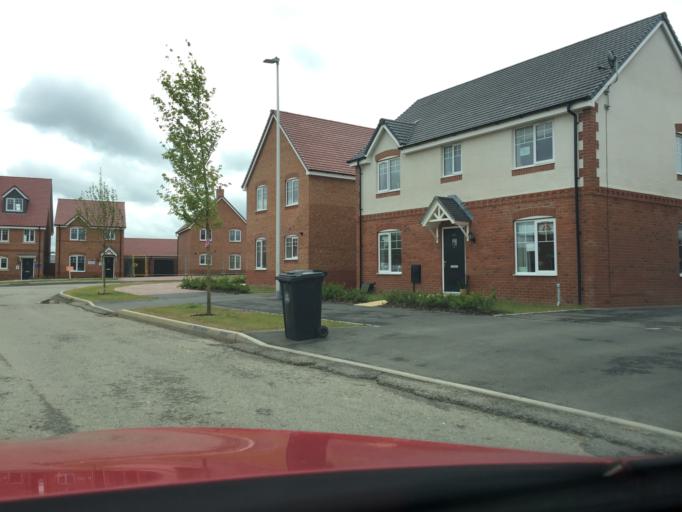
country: GB
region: England
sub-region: Warwickshire
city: Southam
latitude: 52.2509
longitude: -1.3731
